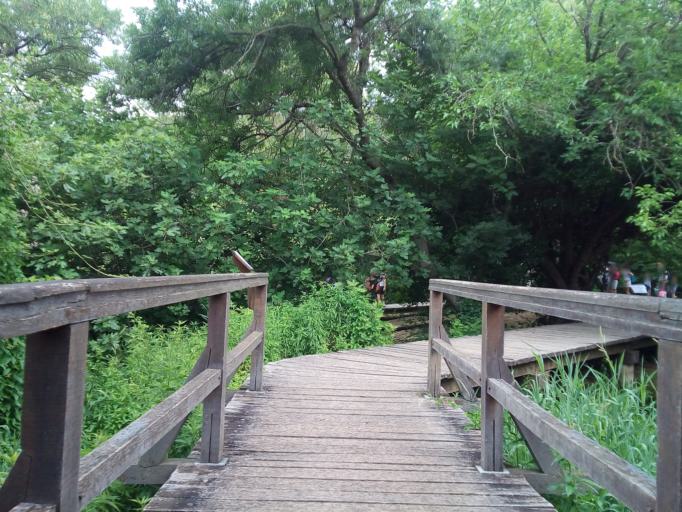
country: HR
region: Sibensko-Kniniska
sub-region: Grad Sibenik
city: Sibenik
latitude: 43.8036
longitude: 15.9665
